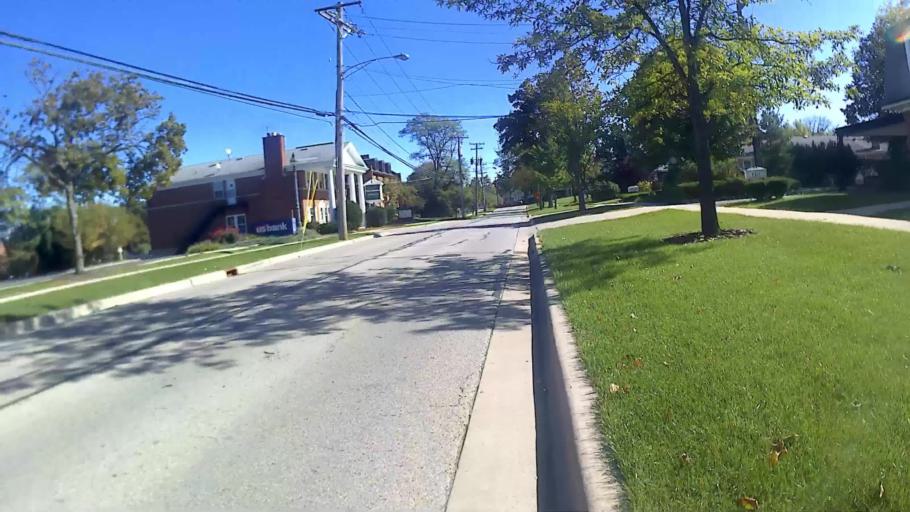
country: US
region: Illinois
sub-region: DuPage County
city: Glen Ellyn
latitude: 41.8755
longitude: -88.0644
